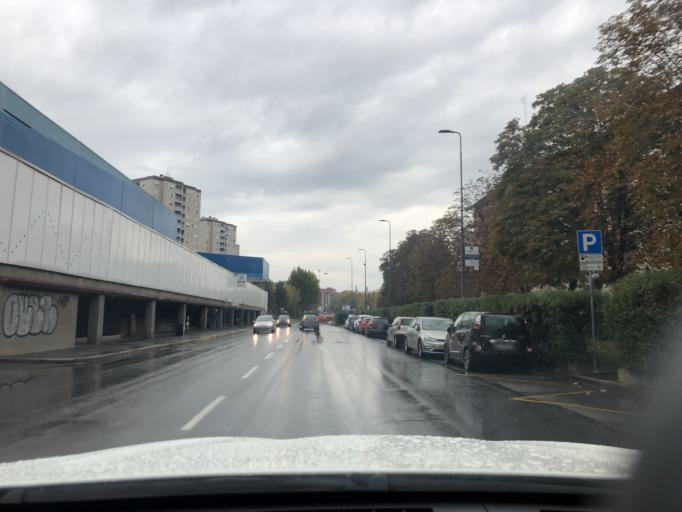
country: IT
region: Lombardy
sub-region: Citta metropolitana di Milano
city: Pero
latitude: 45.4973
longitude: 9.1136
